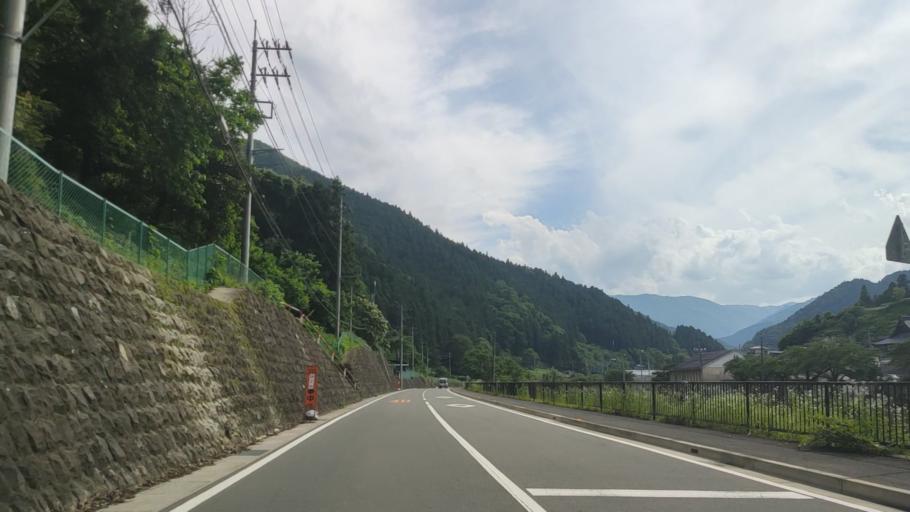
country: JP
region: Gunma
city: Tomioka
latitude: 36.1746
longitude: 138.7371
